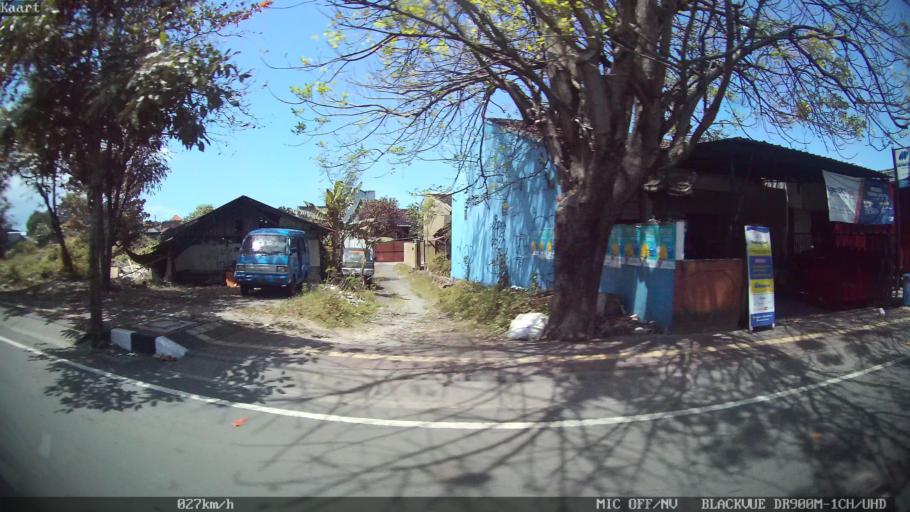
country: ID
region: Bali
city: Denpasar
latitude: -8.6637
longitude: 115.1908
